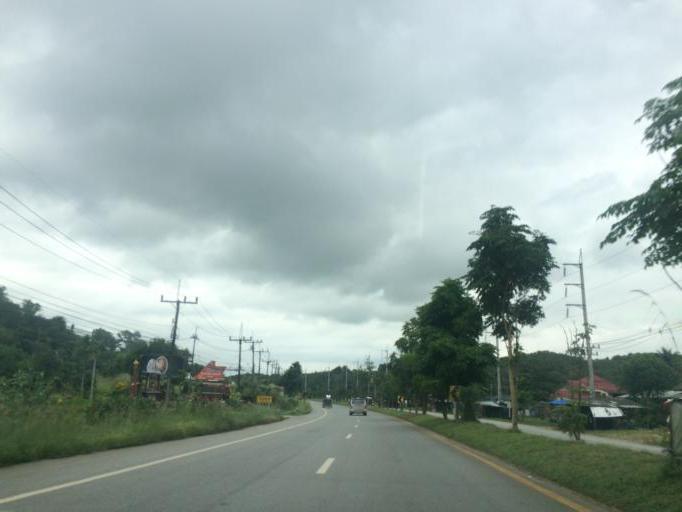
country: TH
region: Chiang Rai
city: Mae Chan
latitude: 20.1232
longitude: 99.8680
